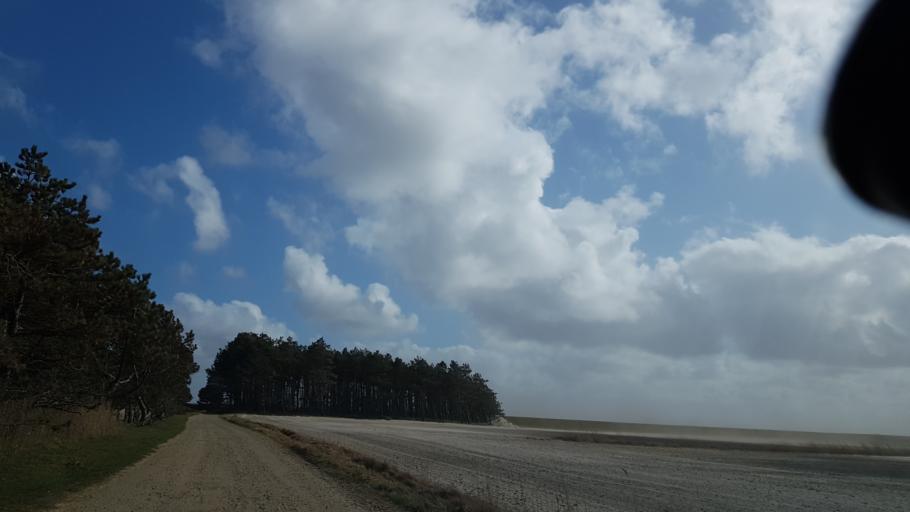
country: DE
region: Schleswig-Holstein
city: List
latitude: 55.0839
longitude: 8.5298
